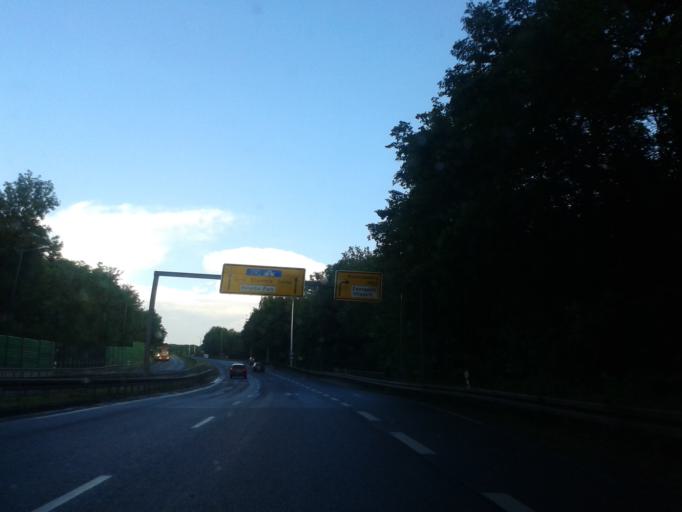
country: DE
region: Saxony
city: Markkleeberg
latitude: 51.3048
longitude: 12.3681
